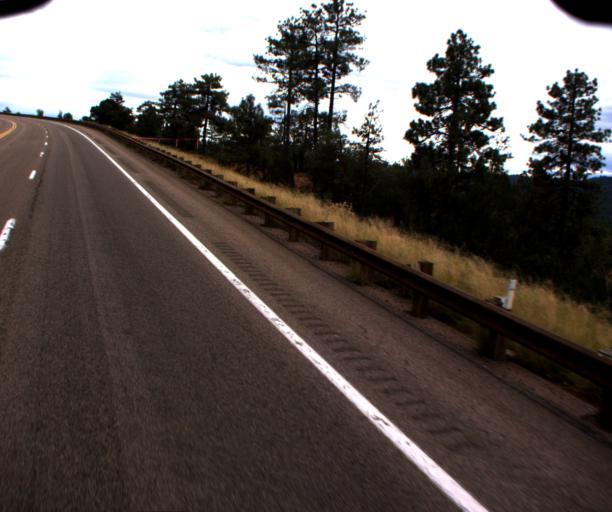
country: US
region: Arizona
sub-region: Gila County
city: Star Valley
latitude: 34.3053
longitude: -110.9448
